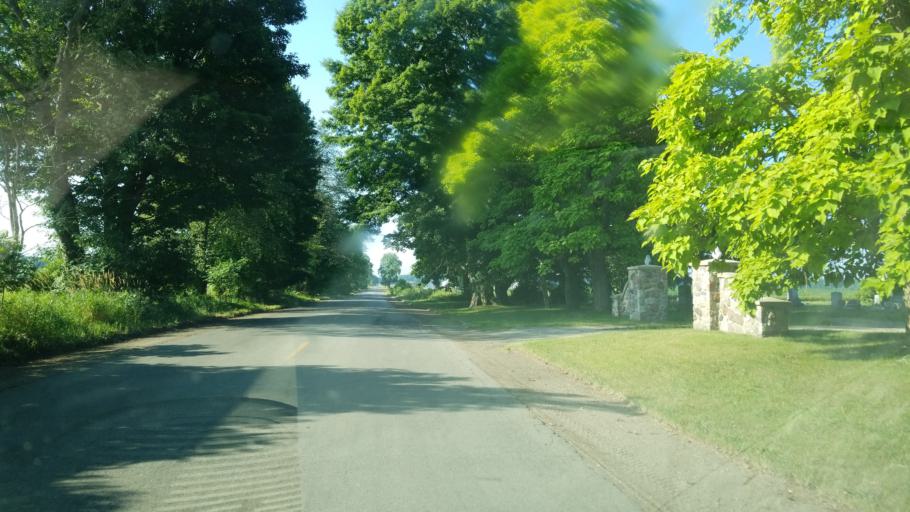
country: US
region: Michigan
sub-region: Mecosta County
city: Canadian Lakes
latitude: 43.5396
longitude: -85.3922
